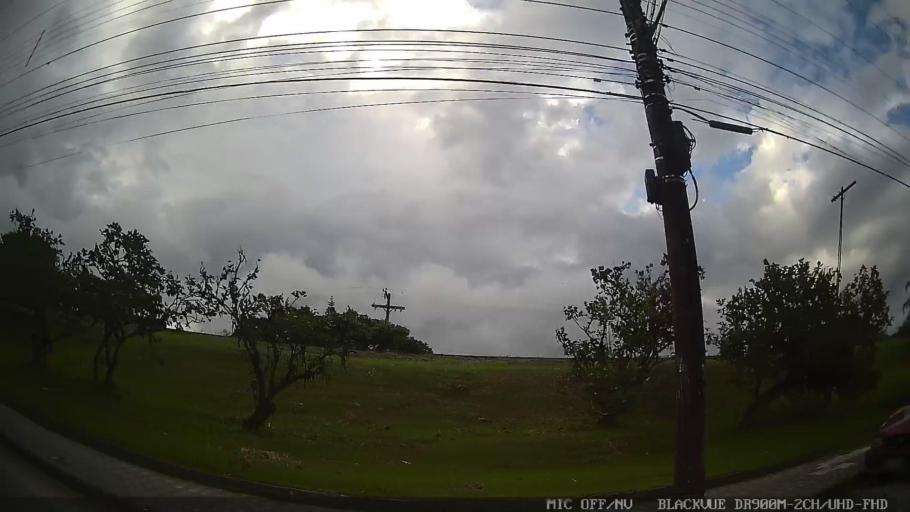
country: BR
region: Sao Paulo
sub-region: Itanhaem
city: Itanhaem
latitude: -24.1866
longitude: -46.7941
